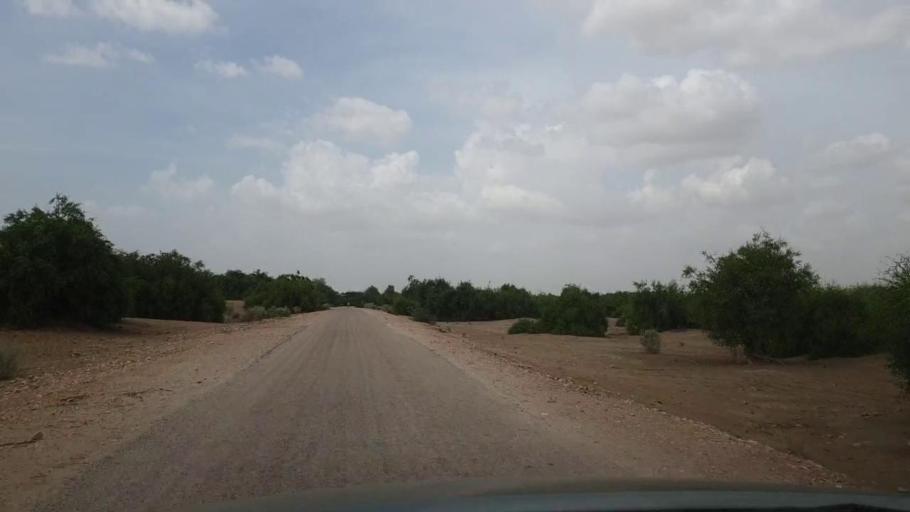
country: PK
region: Sindh
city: Kot Diji
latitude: 27.2187
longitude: 69.0839
